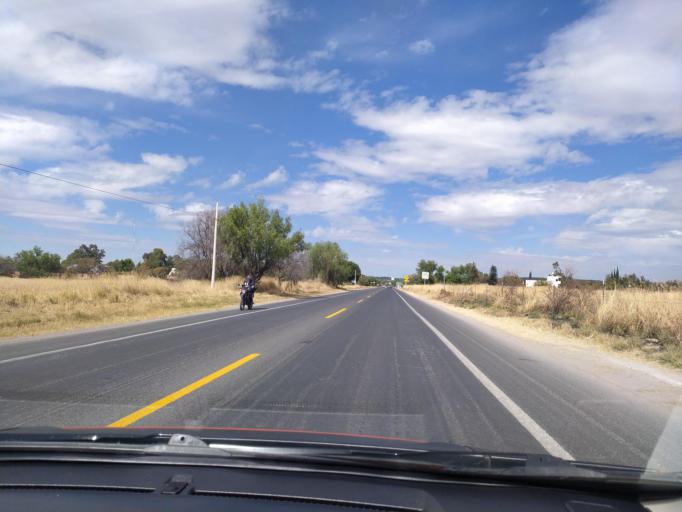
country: LA
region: Oudomxai
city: Muang La
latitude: 21.0176
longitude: 101.8271
